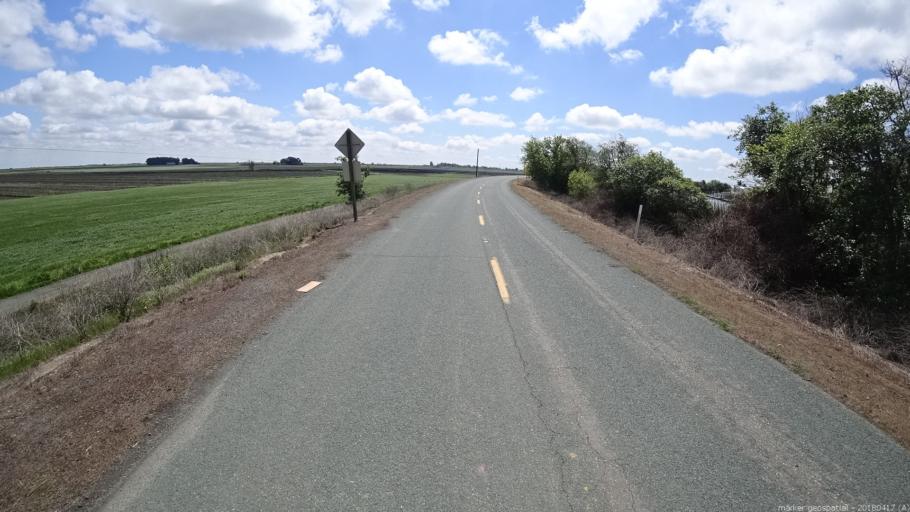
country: US
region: California
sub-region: Solano County
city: Rio Vista
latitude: 38.1494
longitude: -121.5861
